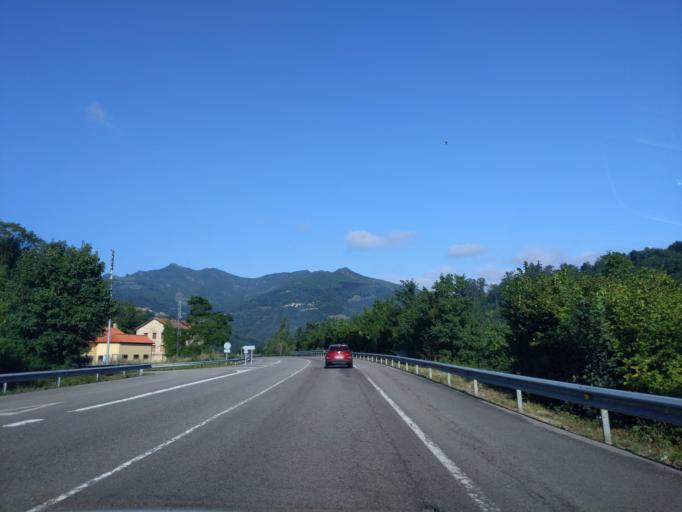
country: ES
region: Asturias
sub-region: Province of Asturias
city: Pola de Laviana
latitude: 43.2362
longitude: -5.5463
